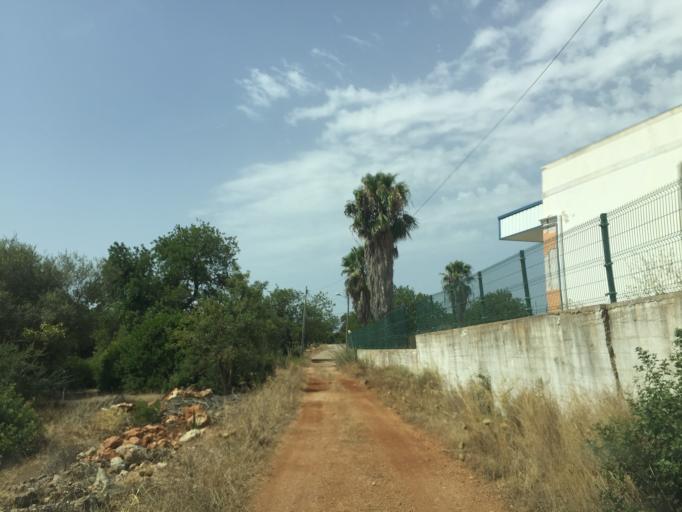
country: PT
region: Faro
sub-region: Loule
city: Boliqueime
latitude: 37.1340
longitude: -8.1397
